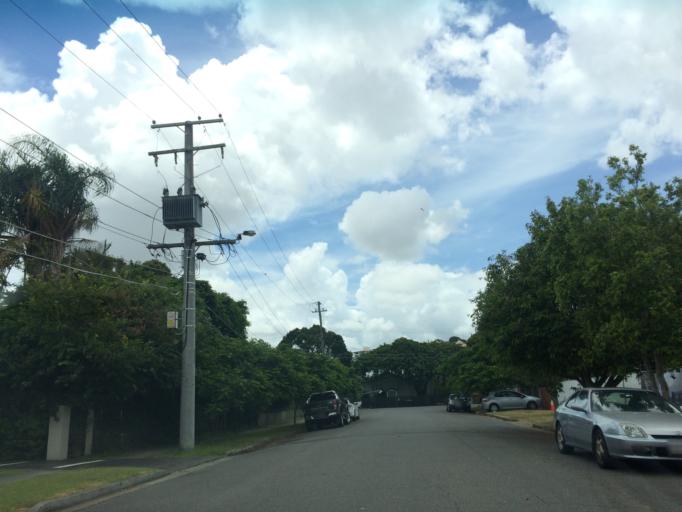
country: AU
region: Queensland
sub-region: Brisbane
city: Ascot
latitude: -27.4438
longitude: 153.0579
